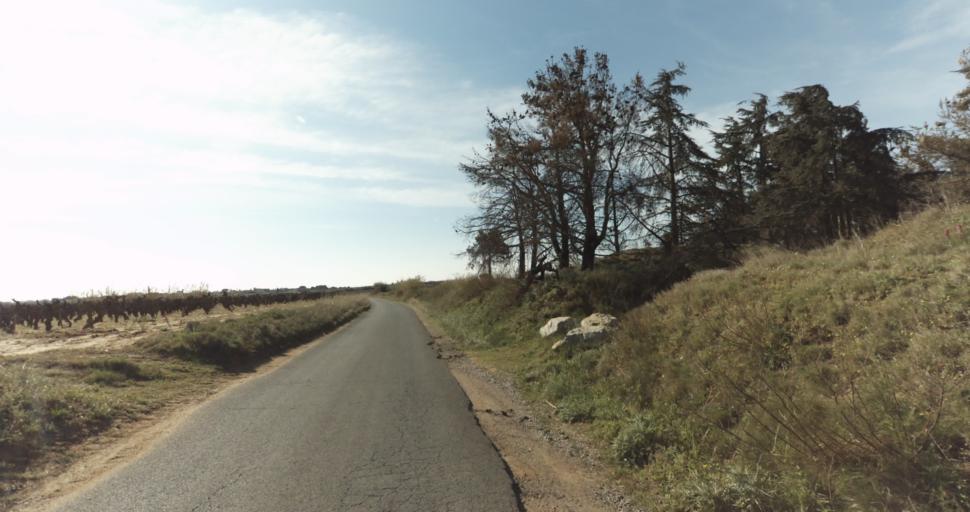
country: FR
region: Languedoc-Roussillon
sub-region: Departement de l'Herault
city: Marseillan
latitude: 43.3438
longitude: 3.5088
